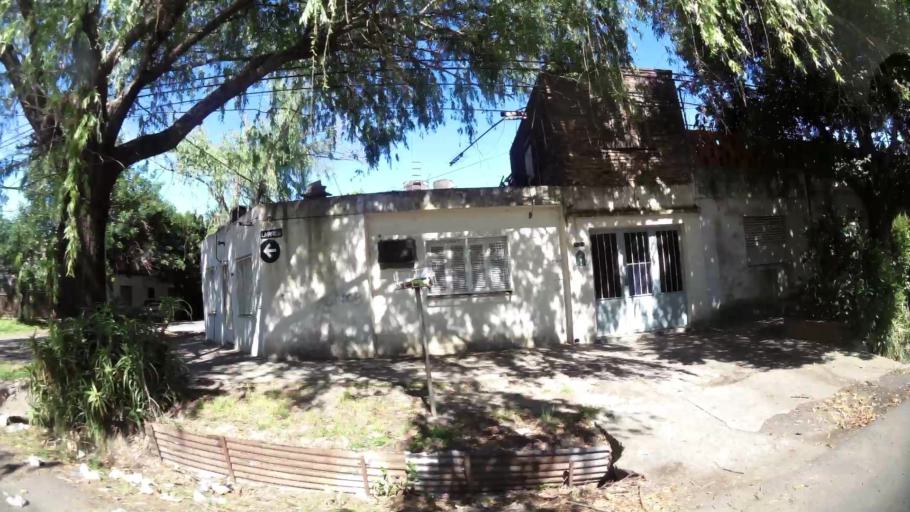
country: AR
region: Santa Fe
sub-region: Departamento de Rosario
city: Rosario
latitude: -32.9652
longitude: -60.6963
